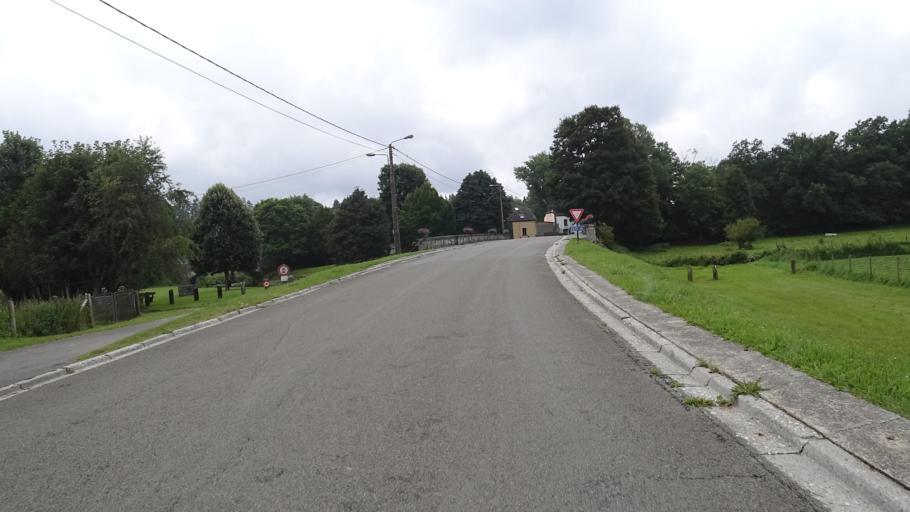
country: BE
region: Wallonia
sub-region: Province du Luxembourg
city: Chiny
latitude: 49.7941
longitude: 5.3807
